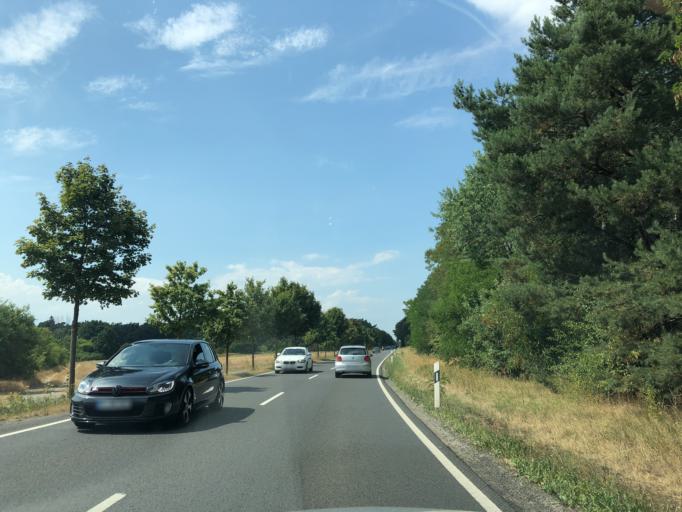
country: DE
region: Hesse
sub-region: Regierungsbezirk Darmstadt
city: Babenhausen
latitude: 49.9755
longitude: 8.9360
